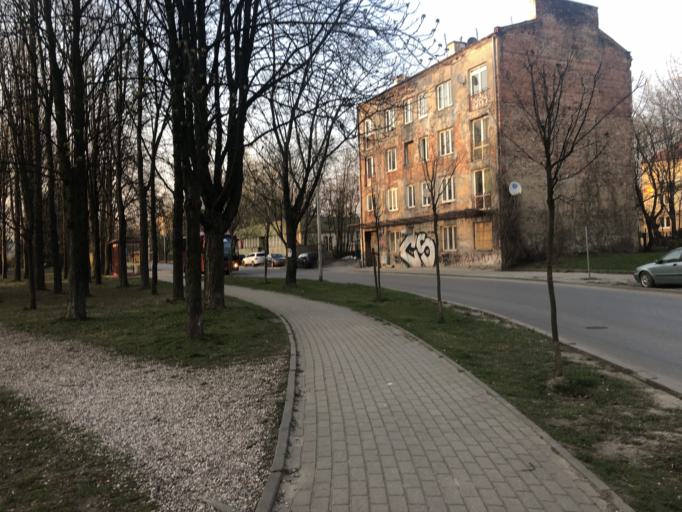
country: PL
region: Masovian Voivodeship
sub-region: Warszawa
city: Ochota
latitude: 52.2244
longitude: 20.9693
